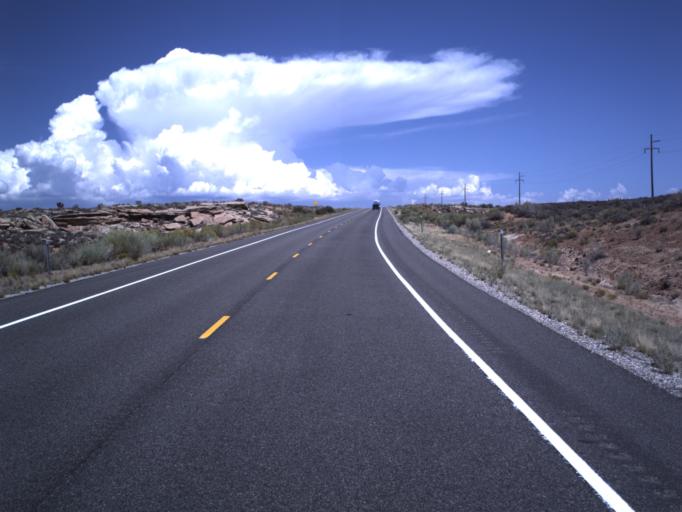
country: US
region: Utah
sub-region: San Juan County
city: Blanding
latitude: 37.3736
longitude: -109.5057
